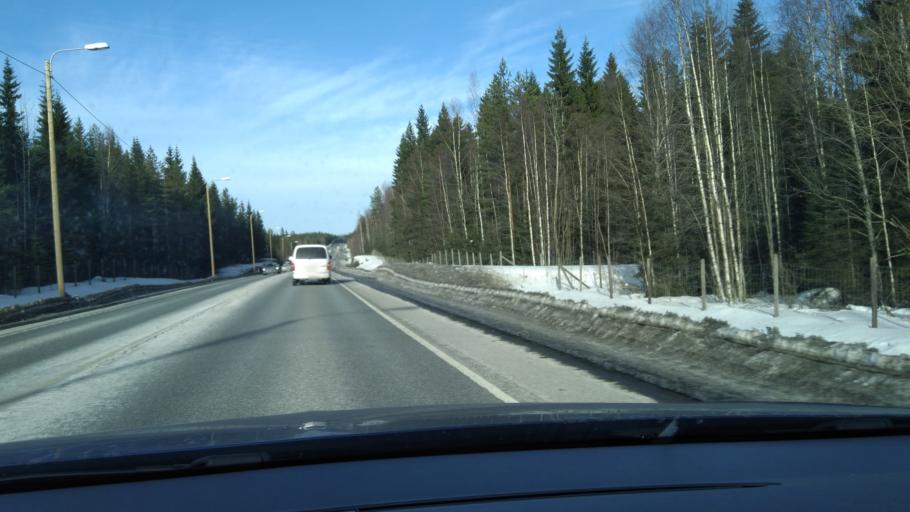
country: FI
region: Pirkanmaa
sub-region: Tampere
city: Orivesi
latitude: 61.6582
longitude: 24.2535
